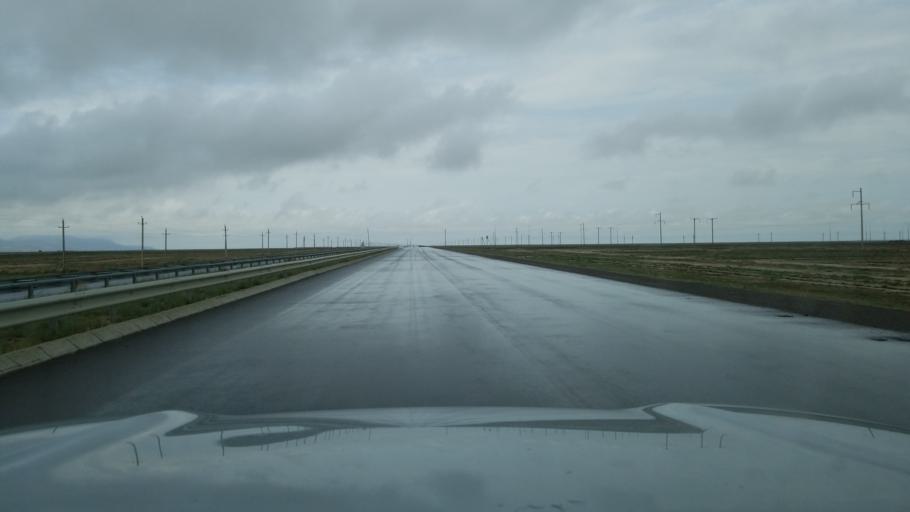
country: TM
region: Balkan
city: Gazanjyk
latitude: 39.1459
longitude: 55.8640
